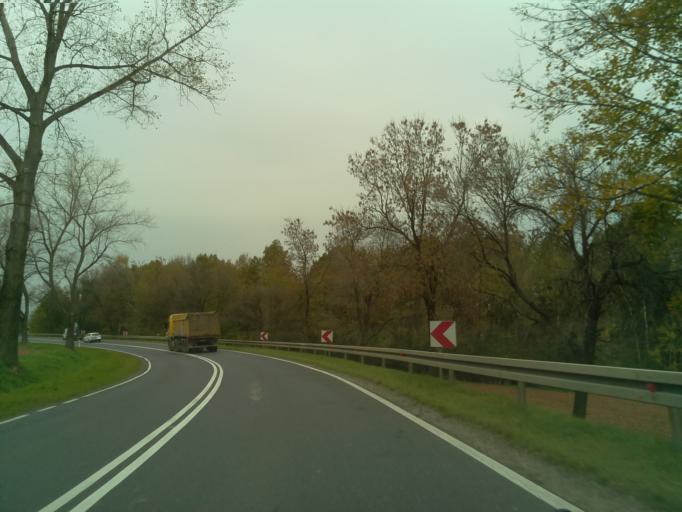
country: PL
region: Lower Silesian Voivodeship
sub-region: Powiat walbrzyski
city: Stare Bogaczowice
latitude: 50.9137
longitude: 16.1959
